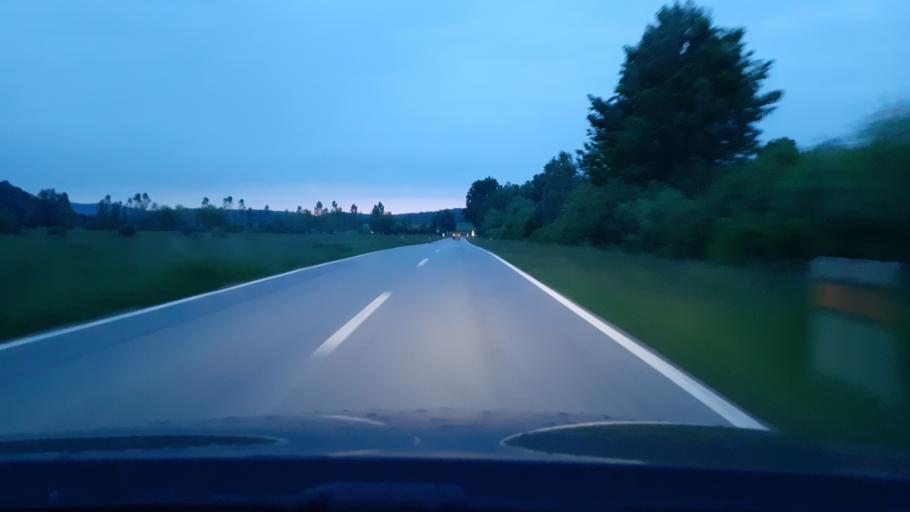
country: HR
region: Pozesko-Slavonska
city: Bilice
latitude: 45.2465
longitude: 17.8381
